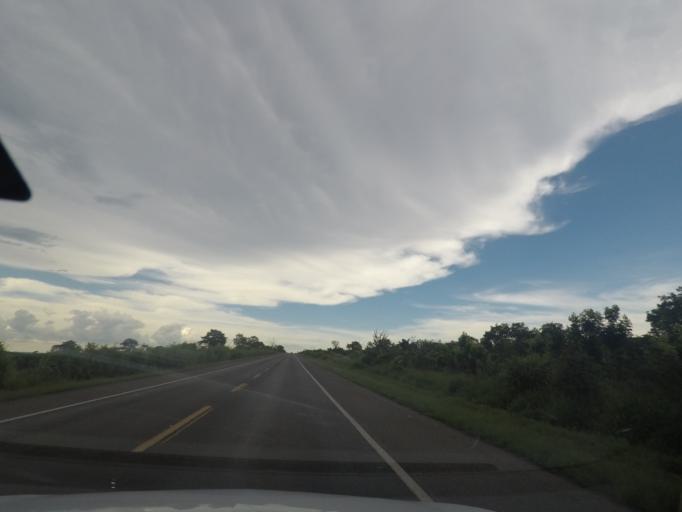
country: BR
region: Minas Gerais
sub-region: Prata
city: Prata
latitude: -19.5891
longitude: -48.8292
